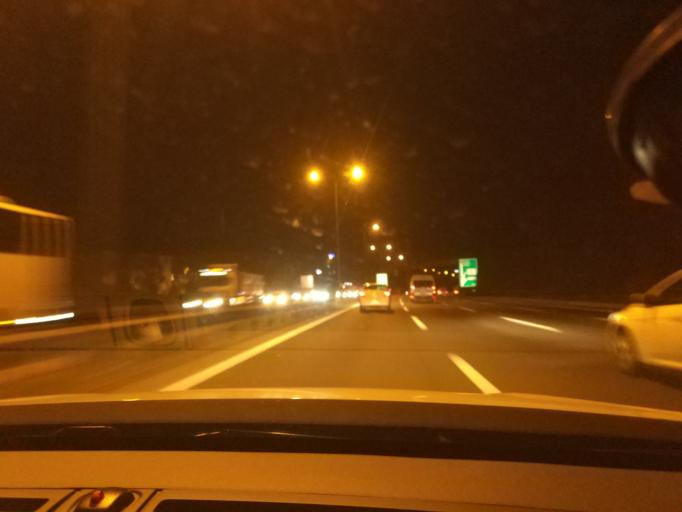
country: TR
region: Istanbul
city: Umraniye
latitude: 41.0922
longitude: 29.0814
